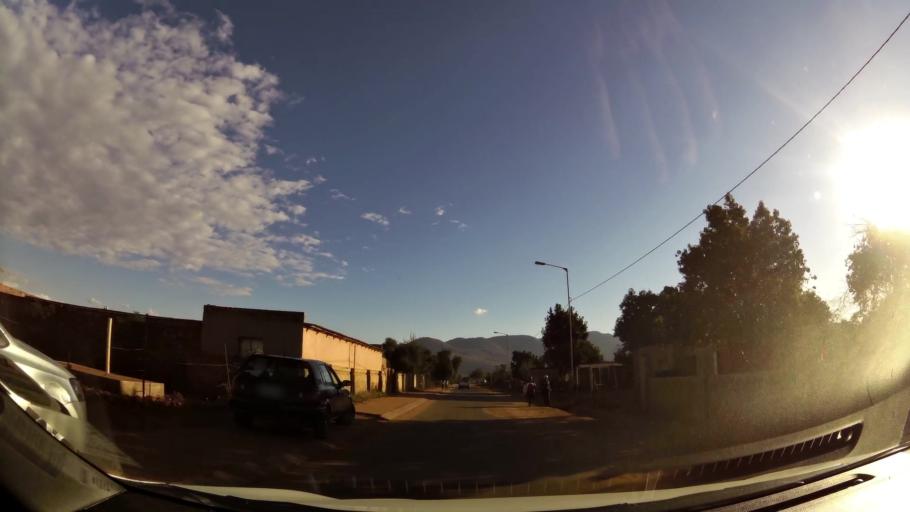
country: ZA
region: Limpopo
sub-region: Waterberg District Municipality
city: Mokopane
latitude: -24.1673
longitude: 28.9861
